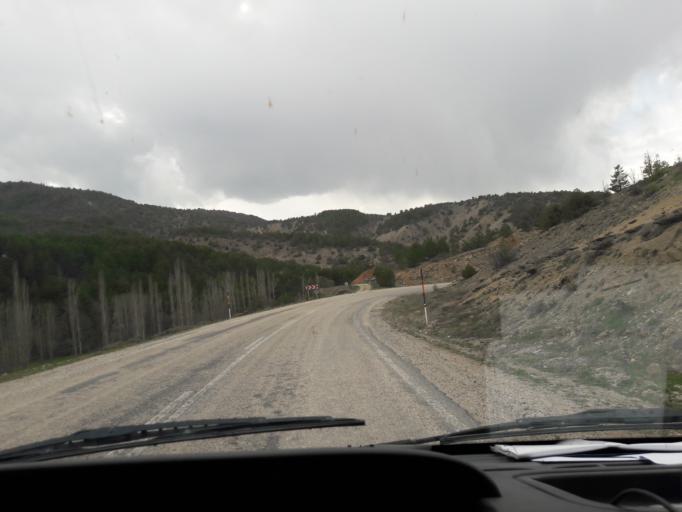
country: TR
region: Giresun
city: Alucra
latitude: 40.2767
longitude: 38.8239
